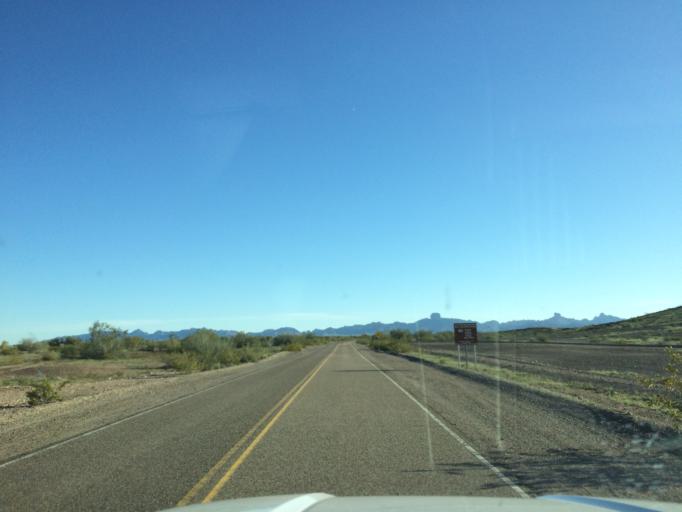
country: US
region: Arizona
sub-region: Yuma County
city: Wellton
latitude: 32.9627
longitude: -114.2921
